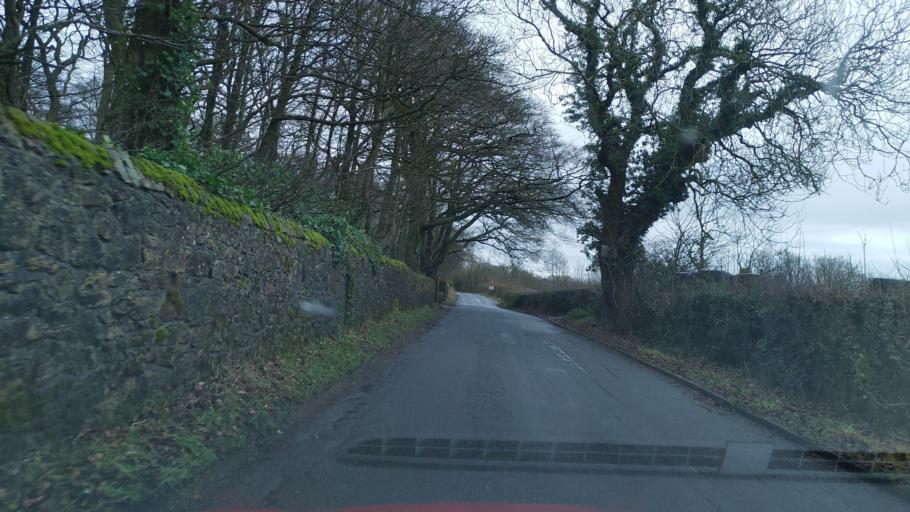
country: GB
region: England
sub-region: Lancashire
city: Clayton-le-Woods
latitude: 53.7054
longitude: -2.6618
